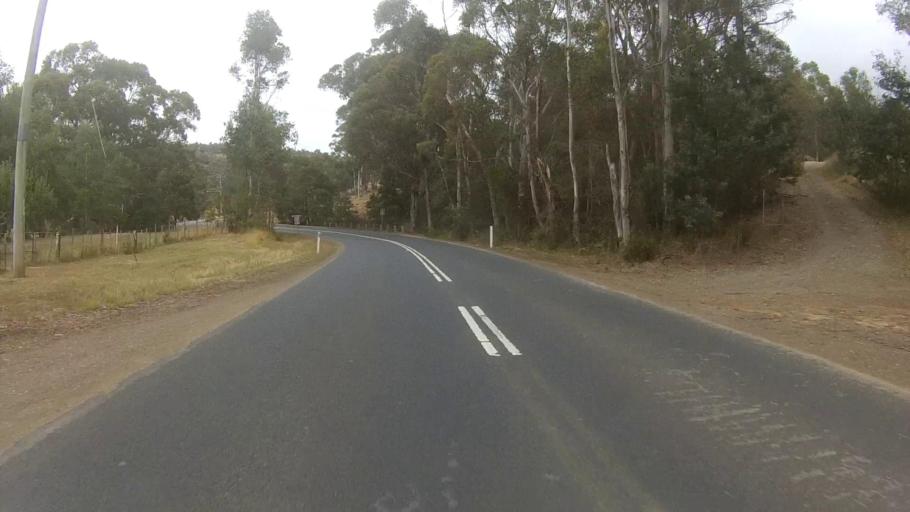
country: AU
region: Tasmania
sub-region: Kingborough
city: Margate
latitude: -43.0123
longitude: 147.2431
